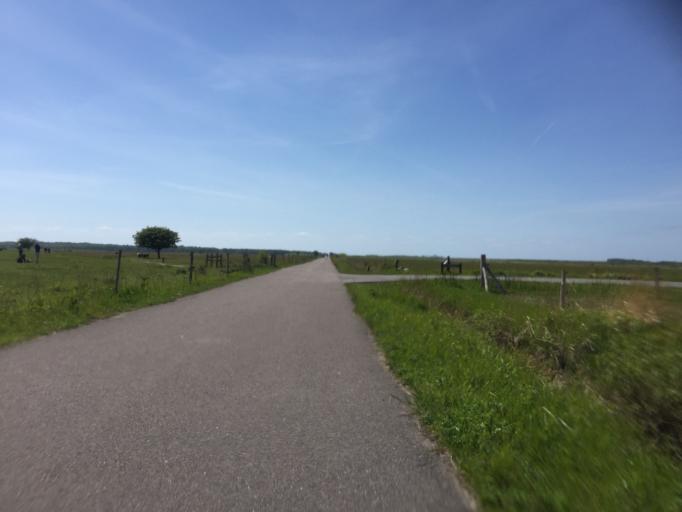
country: DK
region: Capital Region
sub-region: Tarnby Kommune
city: Tarnby
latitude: 55.6123
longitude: 12.5699
